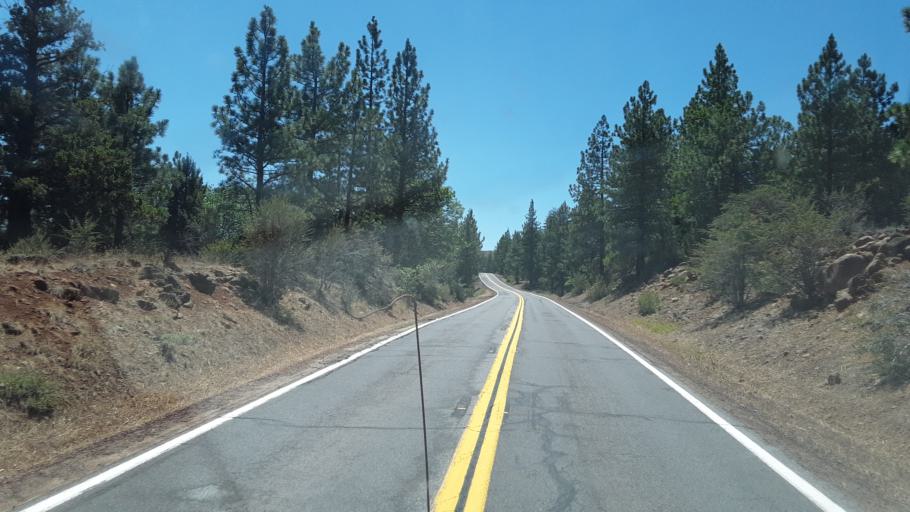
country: US
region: California
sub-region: Lassen County
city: Johnstonville
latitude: 40.4771
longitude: -120.5513
